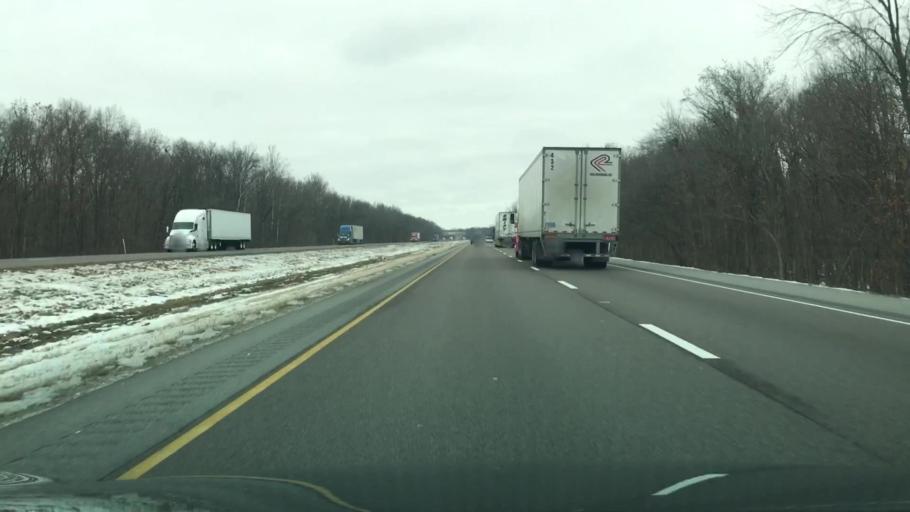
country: US
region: Illinois
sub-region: Jefferson County
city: Mount Vernon
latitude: 38.2348
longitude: -88.9059
